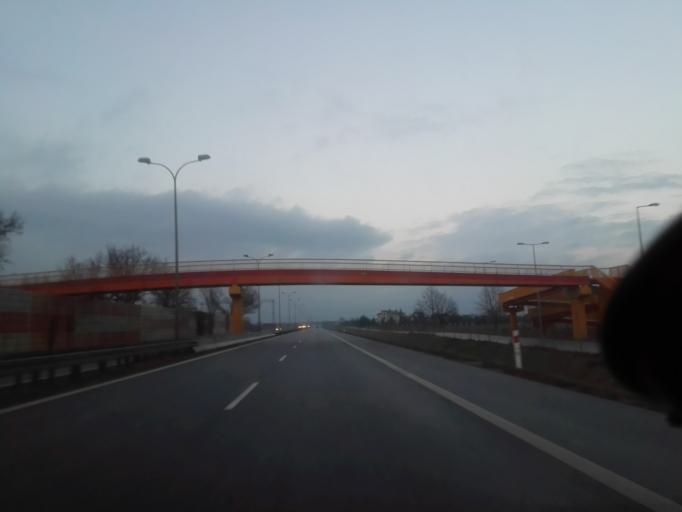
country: PL
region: Masovian Voivodeship
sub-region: Powiat wolominski
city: Dabrowka
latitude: 52.4758
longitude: 21.3343
